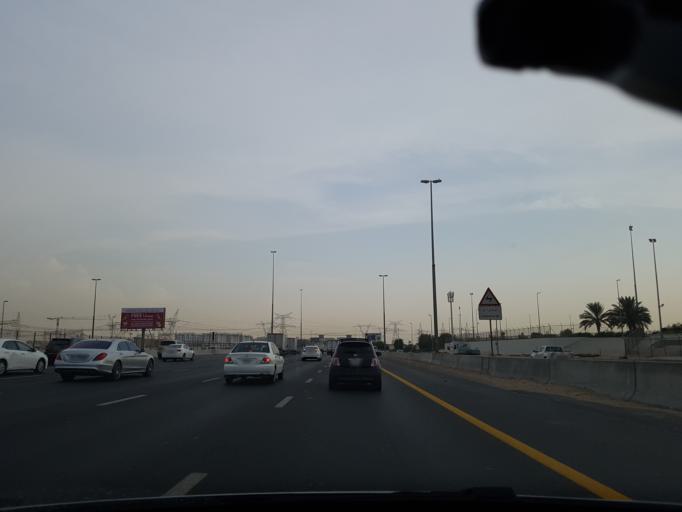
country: AE
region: Ash Shariqah
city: Sharjah
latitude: 25.2288
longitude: 55.4039
